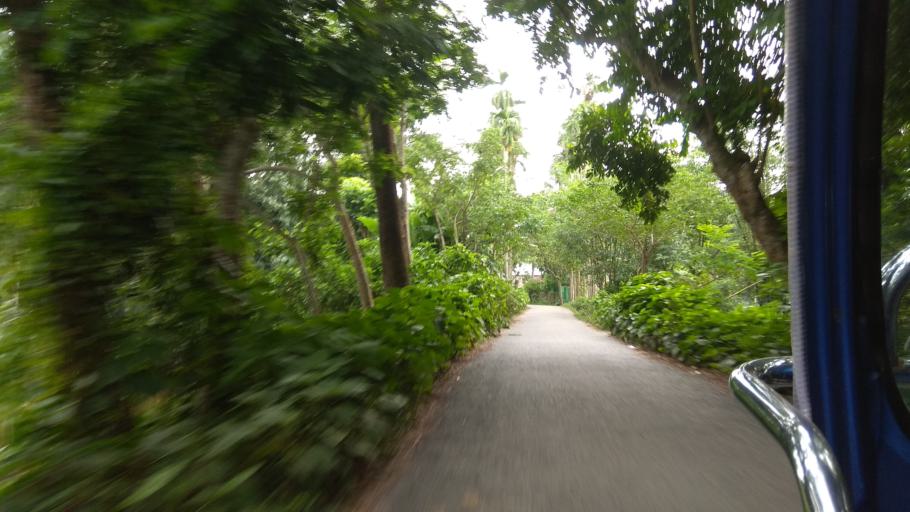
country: BD
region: Khulna
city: Kalia
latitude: 23.0360
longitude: 89.6570
